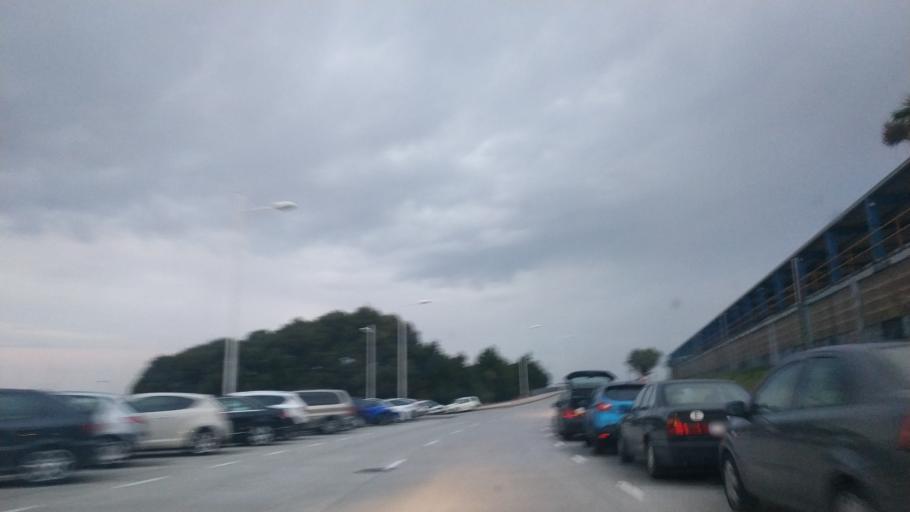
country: ES
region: Galicia
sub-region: Provincia da Coruna
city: A Coruna
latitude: 43.3458
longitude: -8.3906
